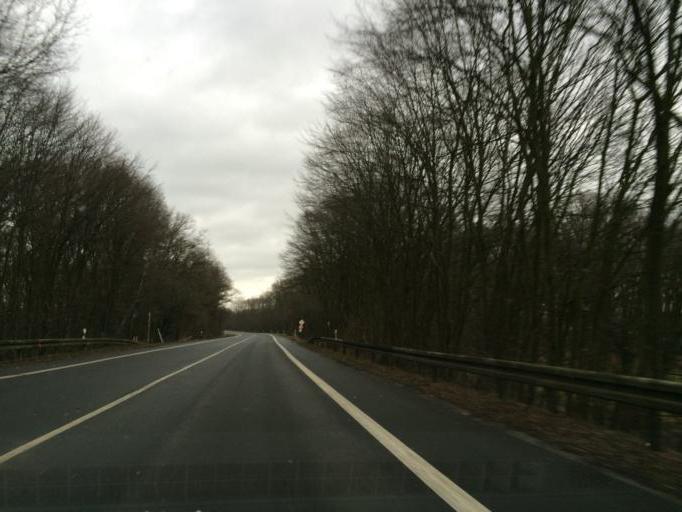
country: DE
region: North Rhine-Westphalia
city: Marl
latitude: 51.6944
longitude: 7.0678
